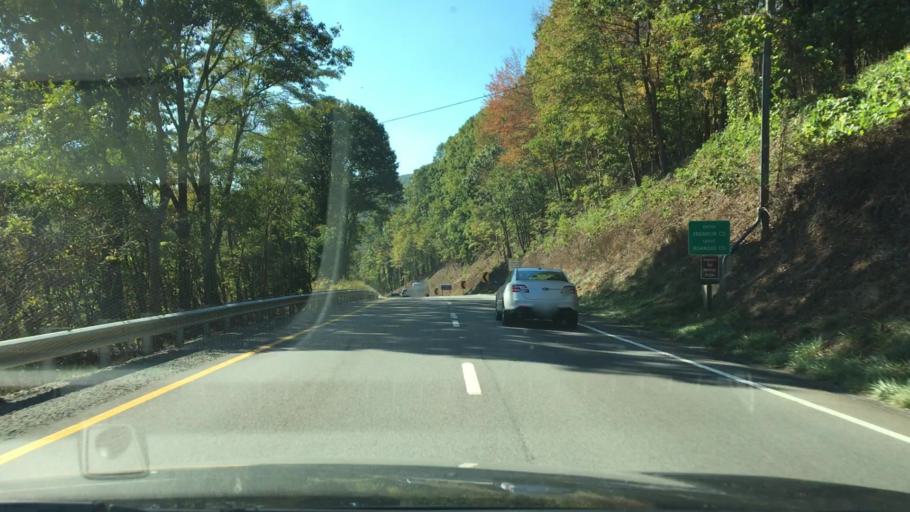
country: US
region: Virginia
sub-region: Roanoke County
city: Narrows
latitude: 37.1399
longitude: -79.9727
